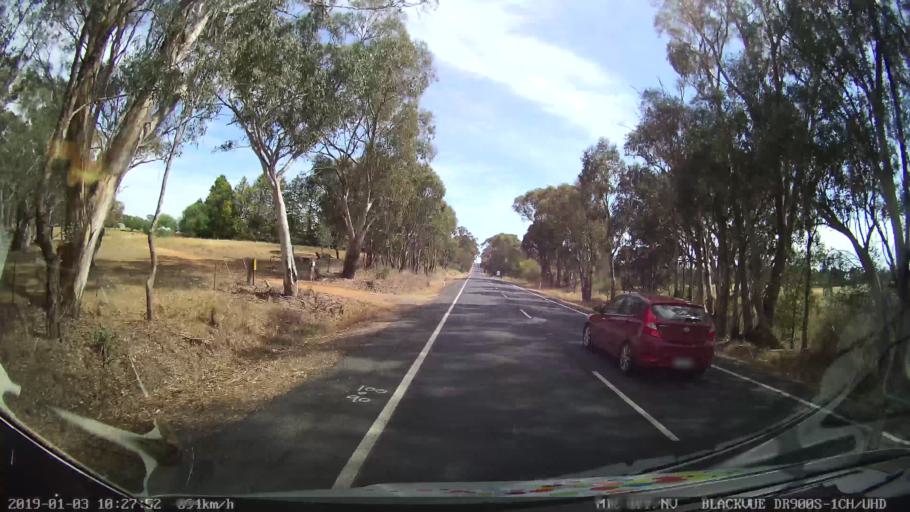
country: AU
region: New South Wales
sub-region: Young
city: Young
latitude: -34.3960
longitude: 148.2586
